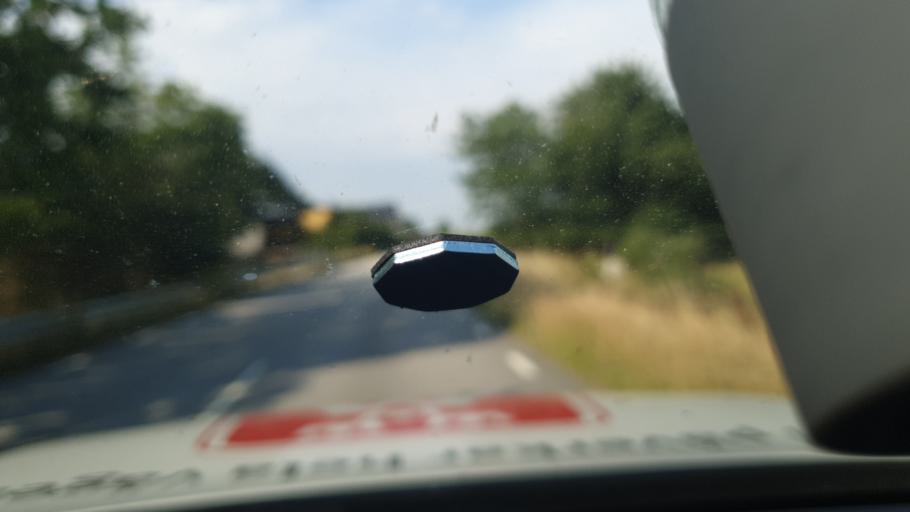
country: SE
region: Skane
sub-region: Trelleborgs Kommun
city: Anderslov
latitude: 55.3981
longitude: 13.2606
